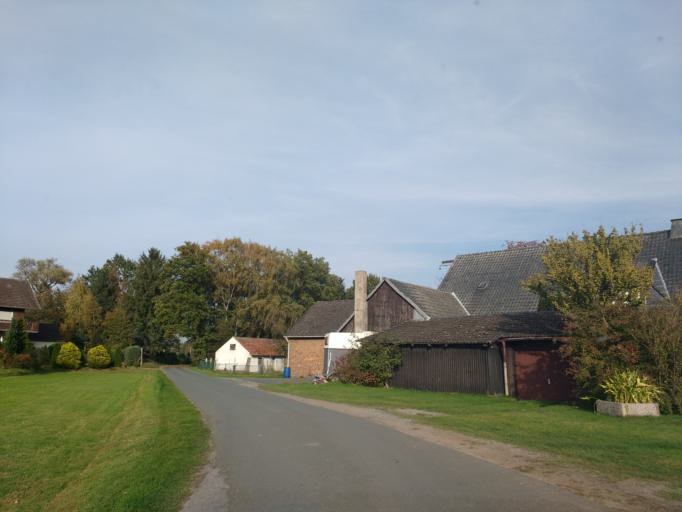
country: DE
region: North Rhine-Westphalia
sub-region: Regierungsbezirk Detmold
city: Hovelhof
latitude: 51.7646
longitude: 8.6377
